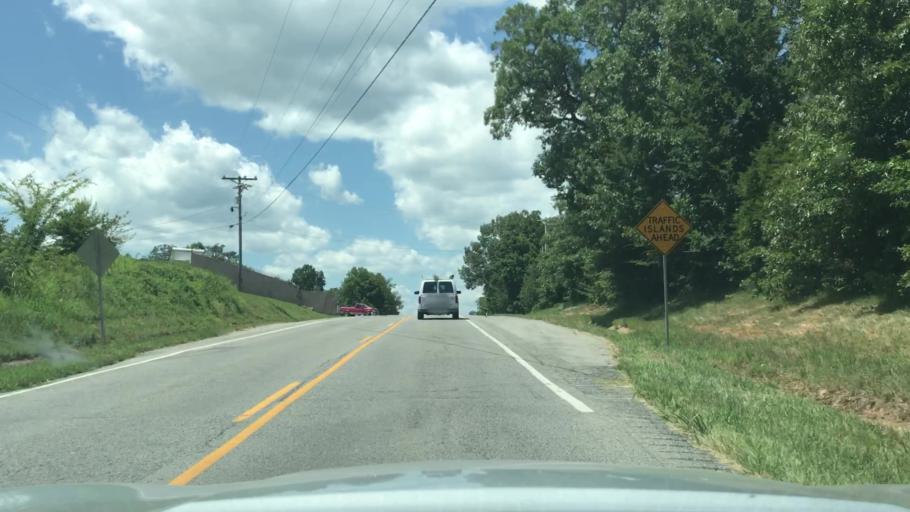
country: US
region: Kentucky
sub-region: Christian County
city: Hopkinsville
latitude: 36.8915
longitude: -87.4622
